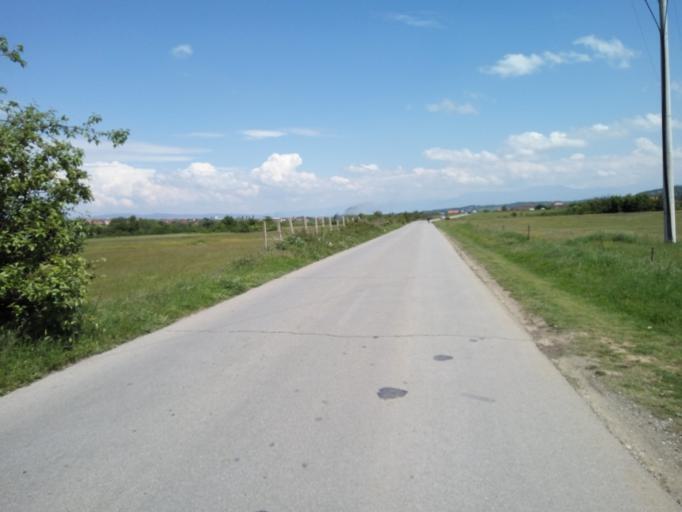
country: XK
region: Gjakova
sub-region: Komuna e Gjakoves
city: Gjakove
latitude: 42.3645
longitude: 20.4245
